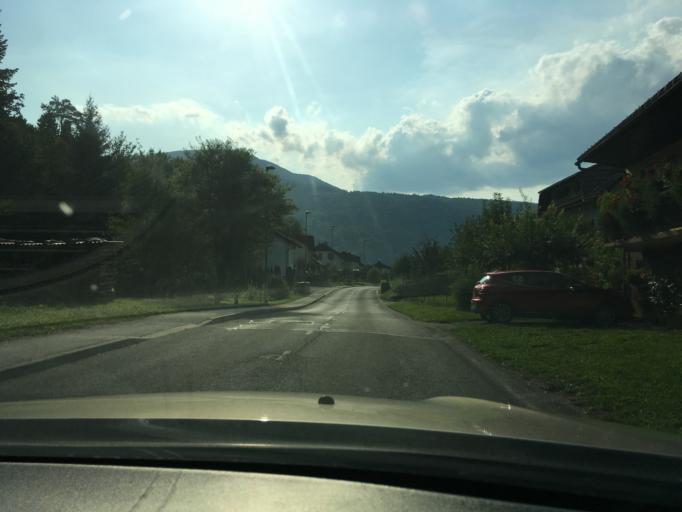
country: SI
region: Dolenjske Toplice
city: Dolenjske Toplice
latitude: 45.7613
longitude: 15.0453
